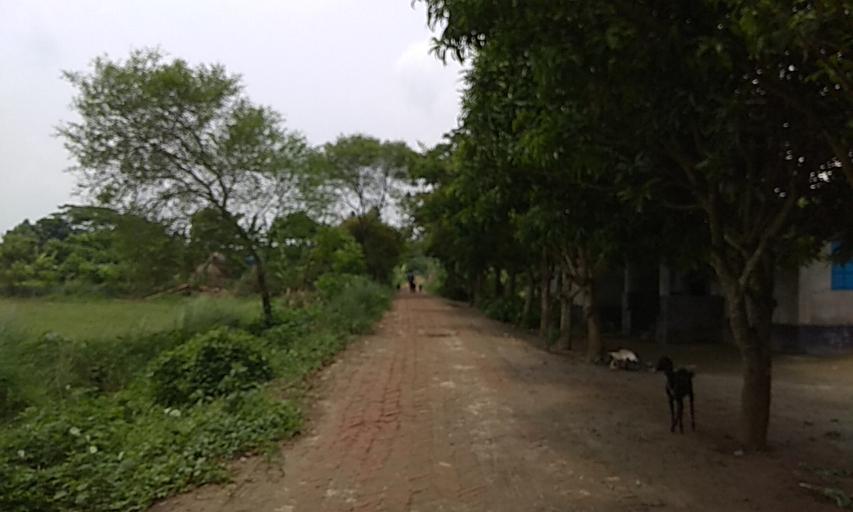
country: BD
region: Dhaka
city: Dohar
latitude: 23.5391
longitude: 89.9912
